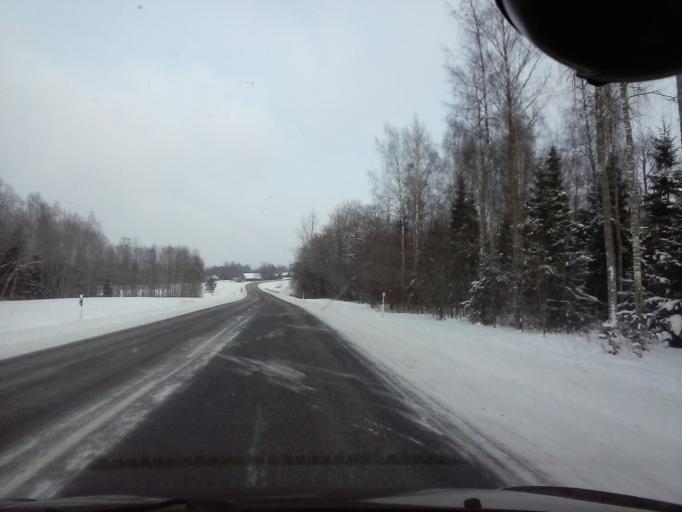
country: EE
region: Paernumaa
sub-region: Saarde vald
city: Kilingi-Nomme
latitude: 58.1714
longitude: 25.0306
